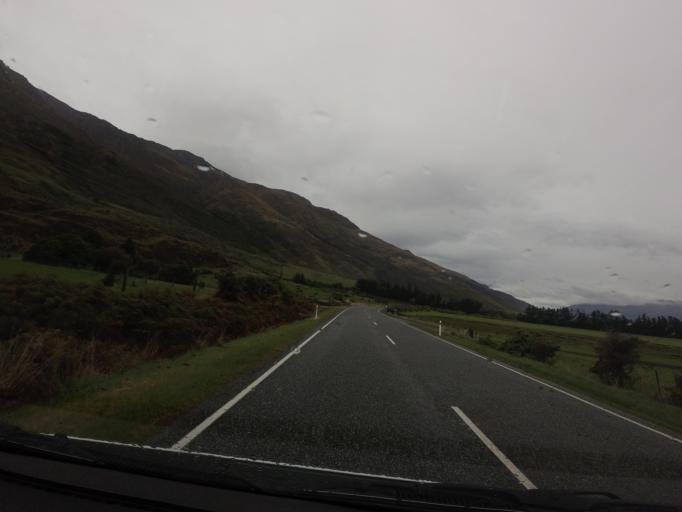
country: NZ
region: Otago
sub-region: Queenstown-Lakes District
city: Wanaka
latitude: -44.2834
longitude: 169.2021
